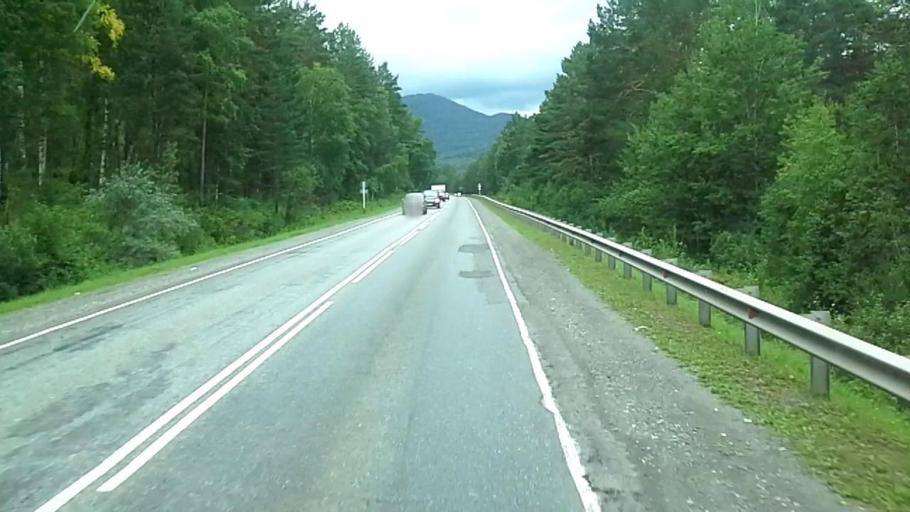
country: RU
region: Altay
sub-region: Mayminskiy Rayon
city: Manzherok
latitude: 51.8095
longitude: 85.7574
